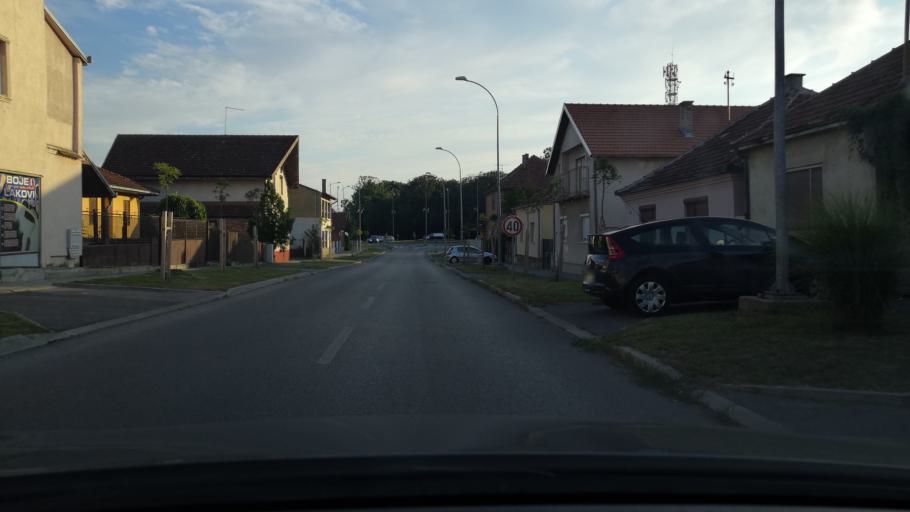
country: RS
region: Autonomna Pokrajina Vojvodina
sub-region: Sremski Okrug
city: Ingija
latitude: 45.0534
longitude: 20.0770
